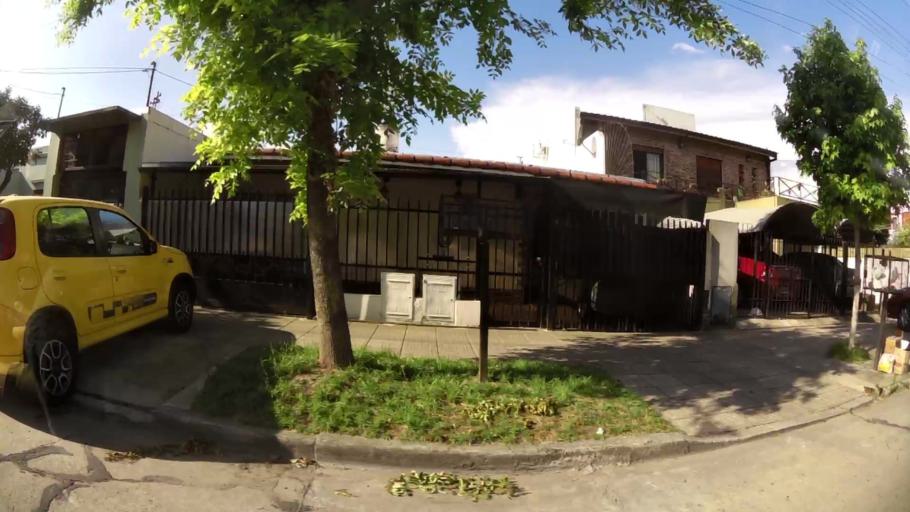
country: AR
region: Buenos Aires
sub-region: Partido de Merlo
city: Merlo
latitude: -34.6571
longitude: -58.7210
